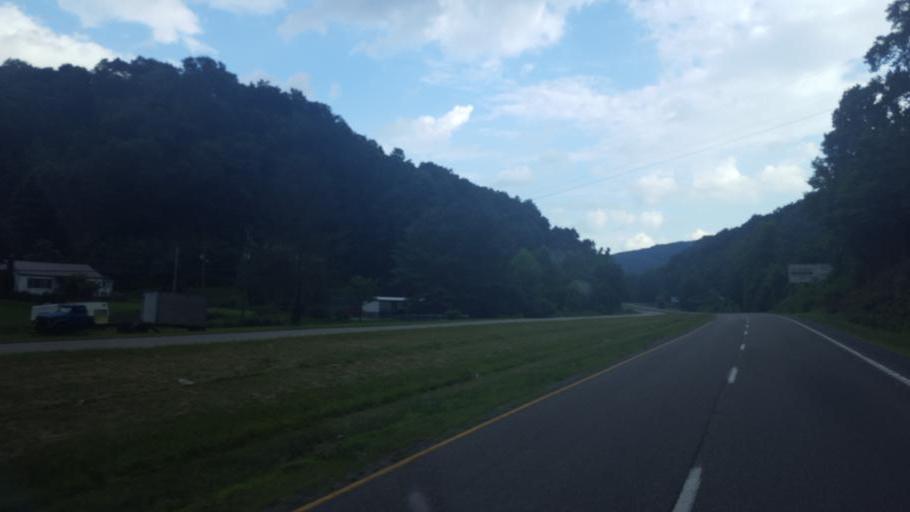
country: US
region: Virginia
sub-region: Wise County
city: Wise
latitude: 37.0461
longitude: -82.6002
